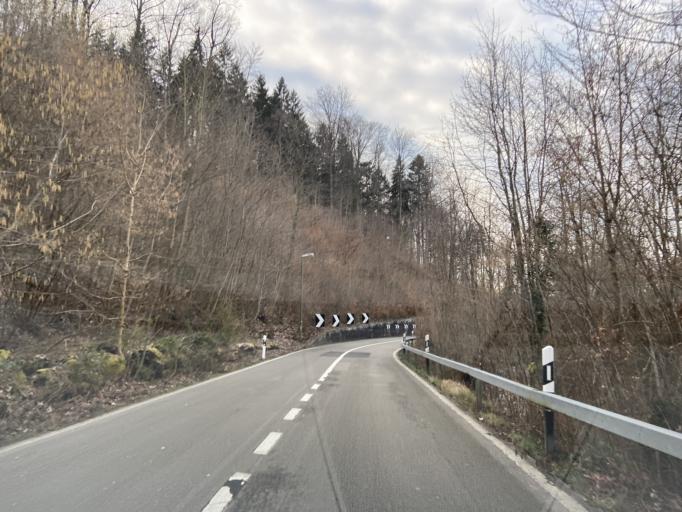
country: CH
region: Zurich
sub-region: Bezirk Winterthur
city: Stadt Winterthur (Kreis 1) / Bruehlberg
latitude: 47.5029
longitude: 8.7092
